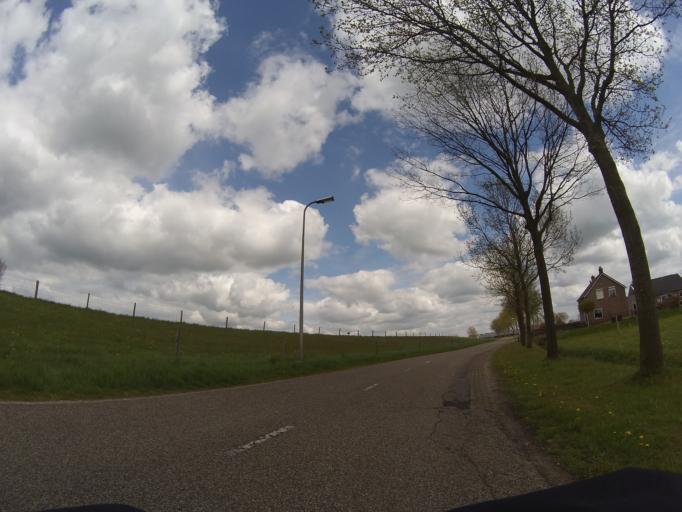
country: NL
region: Overijssel
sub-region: Gemeente Zwolle
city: Zwolle
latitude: 52.5221
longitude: 6.1518
